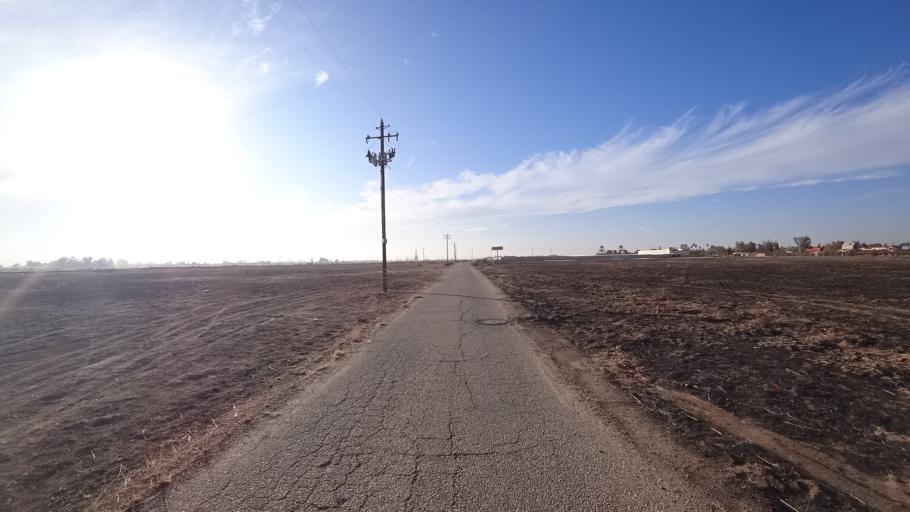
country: US
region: California
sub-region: Kern County
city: Oildale
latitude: 35.4106
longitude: -119.0566
